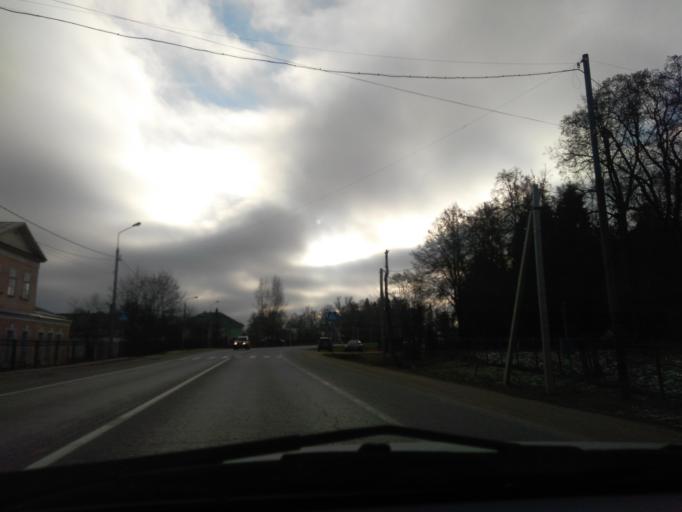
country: RU
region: Moskovskaya
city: Troitsk
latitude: 55.3155
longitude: 37.1534
